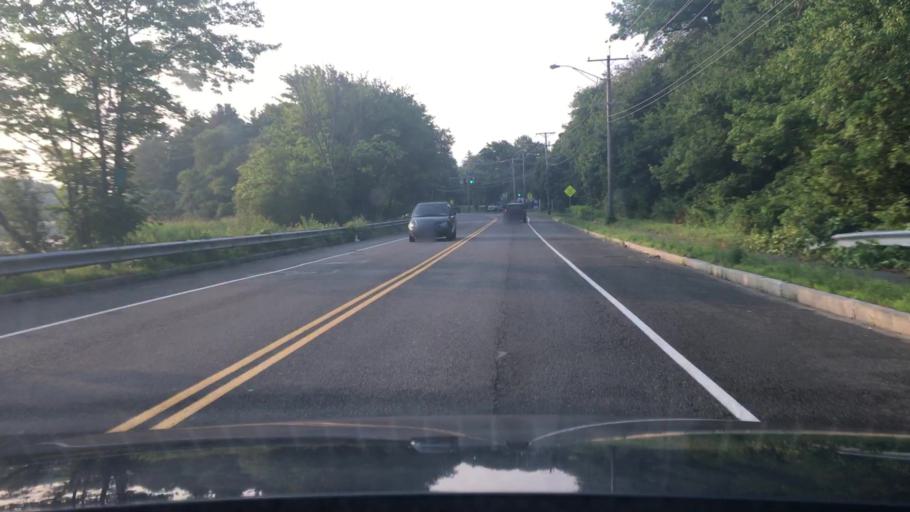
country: US
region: Massachusetts
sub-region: Essex County
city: Saugus
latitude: 42.4781
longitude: -71.0035
